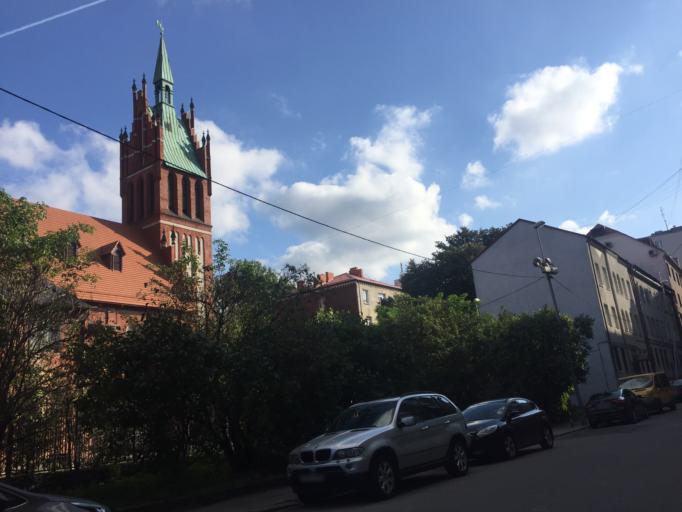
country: RU
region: Kaliningrad
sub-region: Gorod Kaliningrad
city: Kaliningrad
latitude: 54.6982
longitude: 20.5088
